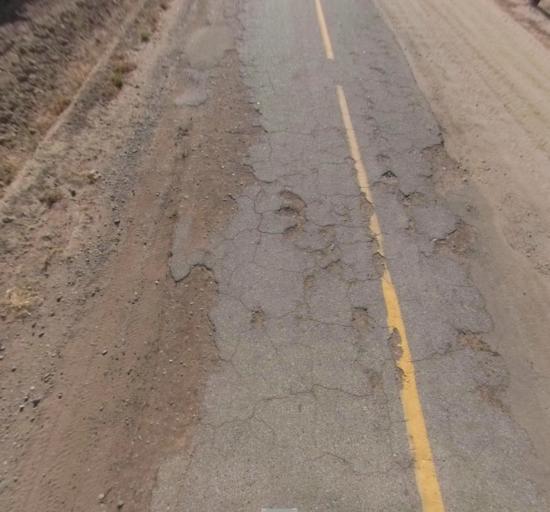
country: US
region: California
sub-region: Fresno County
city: Biola
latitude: 36.8440
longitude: -120.1089
